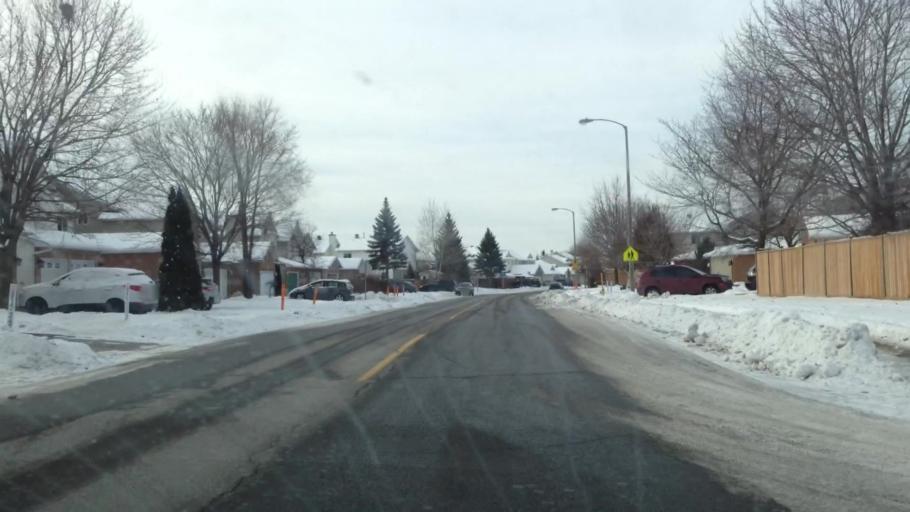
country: CA
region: Ontario
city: Clarence-Rockland
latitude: 45.4701
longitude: -75.4712
